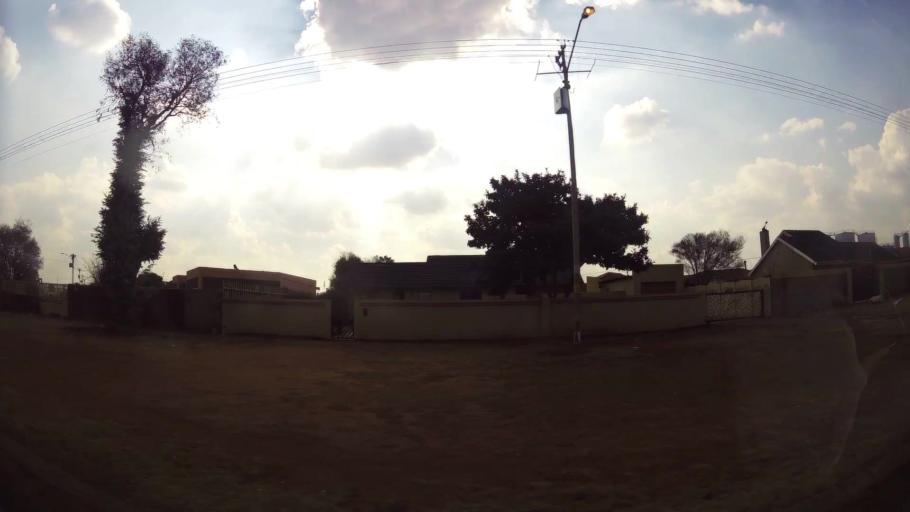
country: ZA
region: Gauteng
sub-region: Ekurhuleni Metropolitan Municipality
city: Germiston
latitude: -26.3025
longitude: 28.1845
